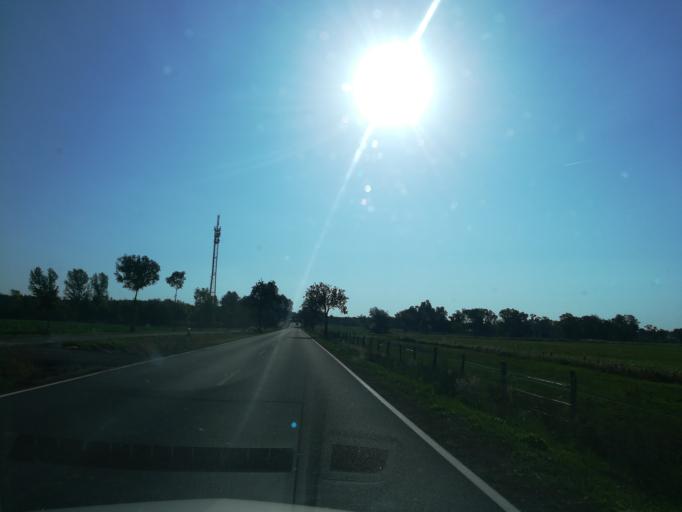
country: DE
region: Saxony-Anhalt
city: Wahlitz
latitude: 52.1129
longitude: 11.7755
